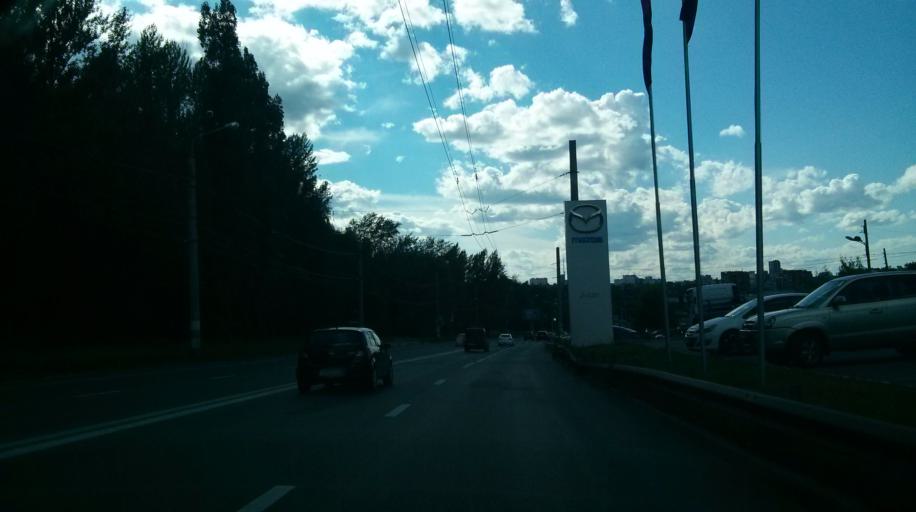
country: RU
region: Nizjnij Novgorod
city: Afonino
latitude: 56.3002
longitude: 44.0622
